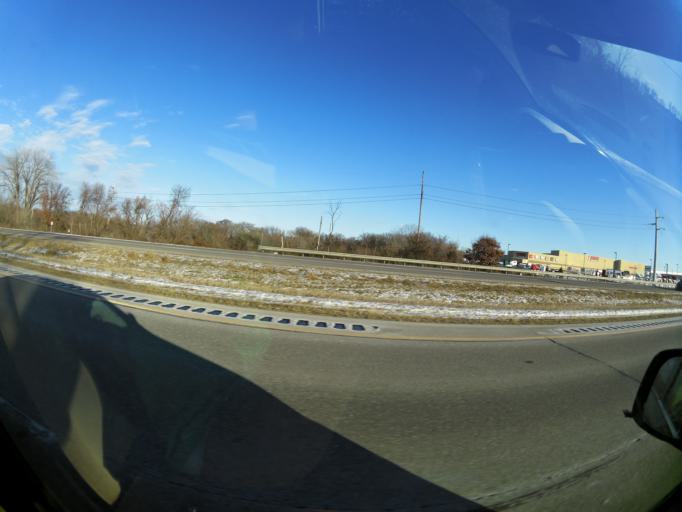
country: US
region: Minnesota
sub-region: Dakota County
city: Inver Grove Heights
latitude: 44.7886
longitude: -93.0352
